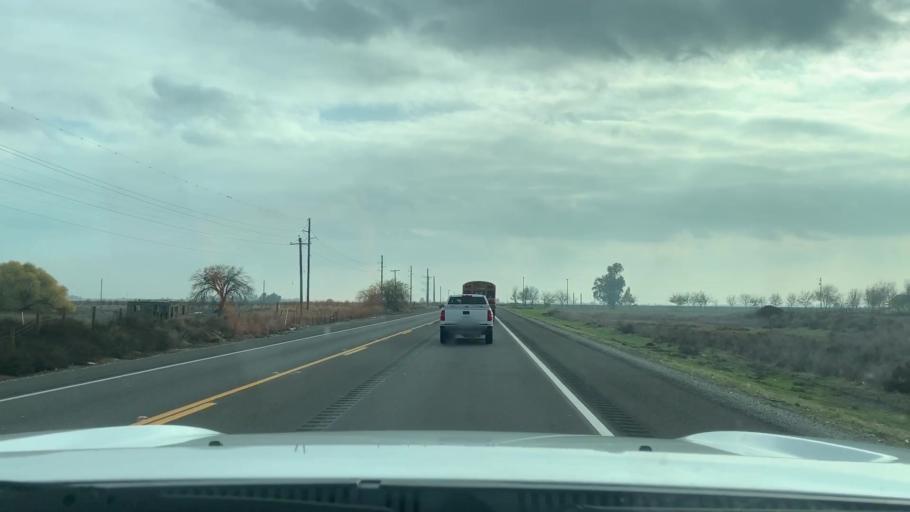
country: US
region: California
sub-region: Kings County
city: Stratford
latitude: 36.2384
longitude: -119.8165
